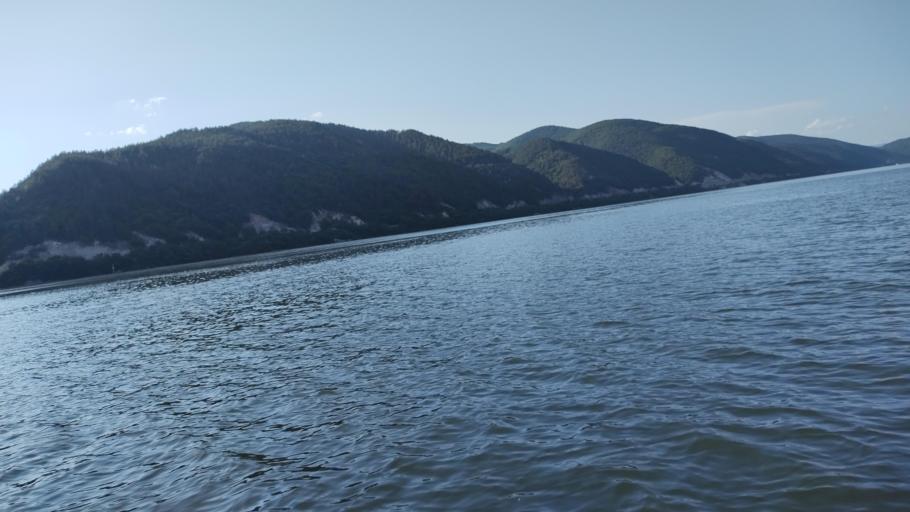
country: RO
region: Mehedinti
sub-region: Comuna Dubova
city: Dubova
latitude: 44.5268
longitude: 22.2096
